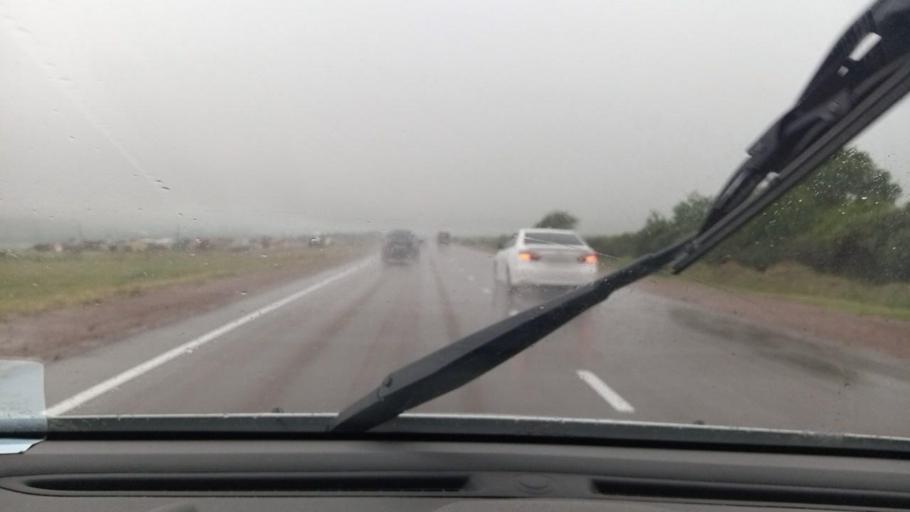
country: UZ
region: Toshkent
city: Angren
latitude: 41.0479
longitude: 70.1559
